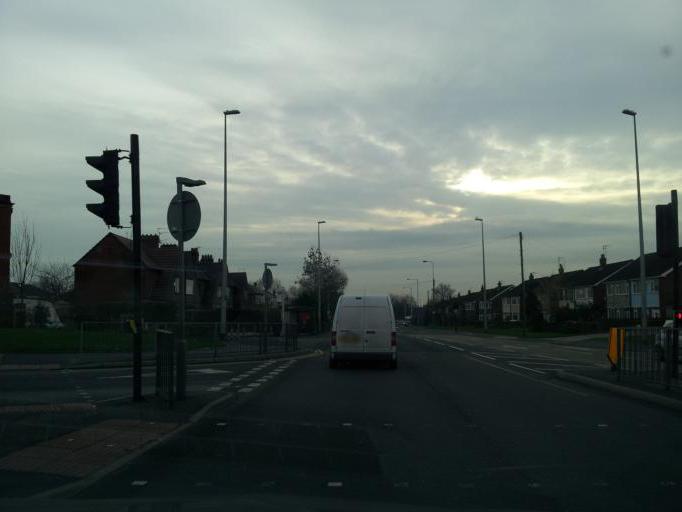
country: GB
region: England
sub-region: Manchester
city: Failsworth
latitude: 53.5341
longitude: -2.1525
